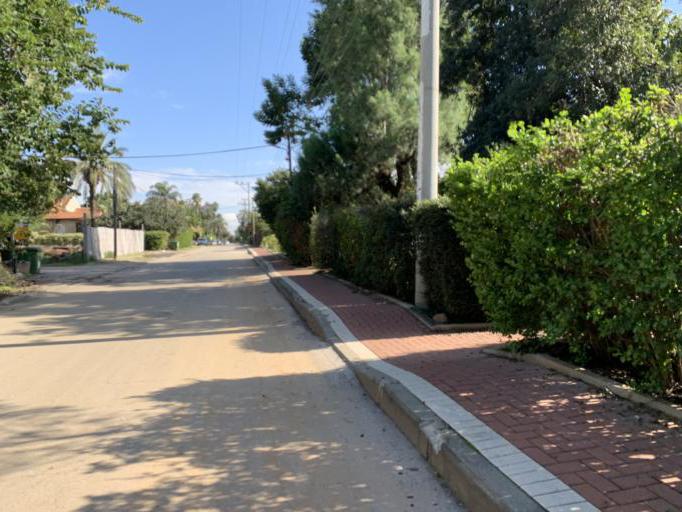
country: IL
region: Central District
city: Ra'anana
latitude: 32.1668
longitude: 34.8687
